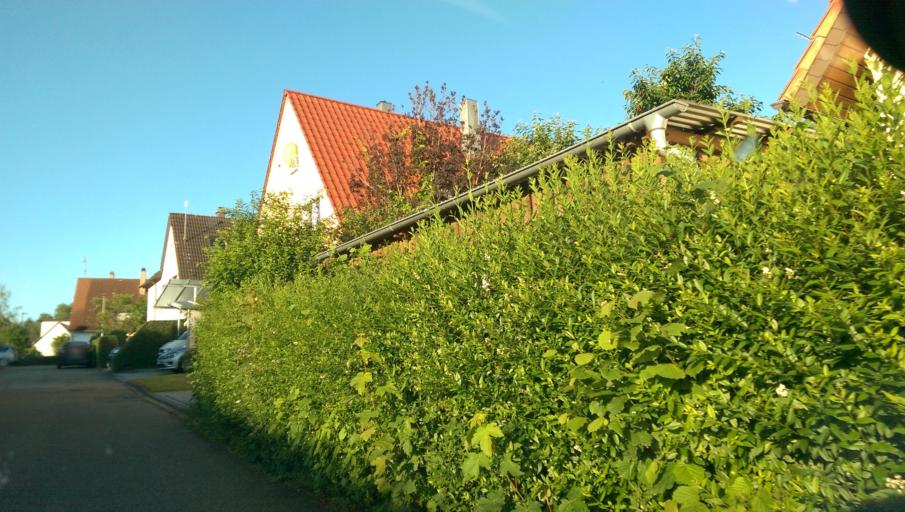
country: DE
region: Baden-Wuerttemberg
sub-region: Karlsruhe Region
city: Dobel
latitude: 48.8566
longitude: 8.5193
